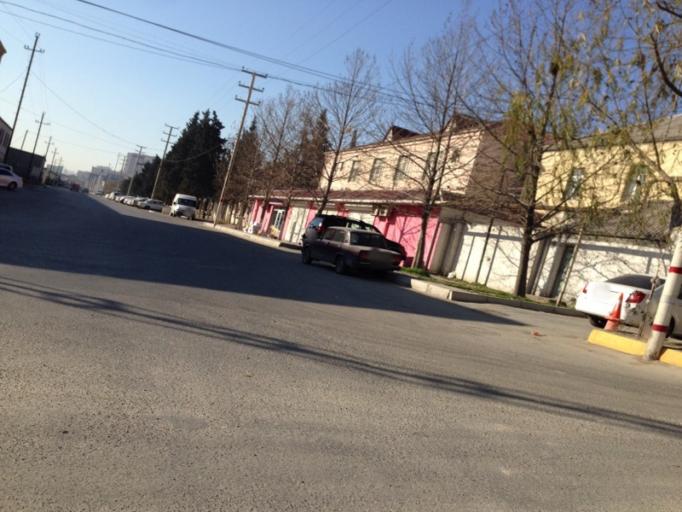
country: AZ
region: Baki
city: Baku
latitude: 40.4230
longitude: 49.8625
